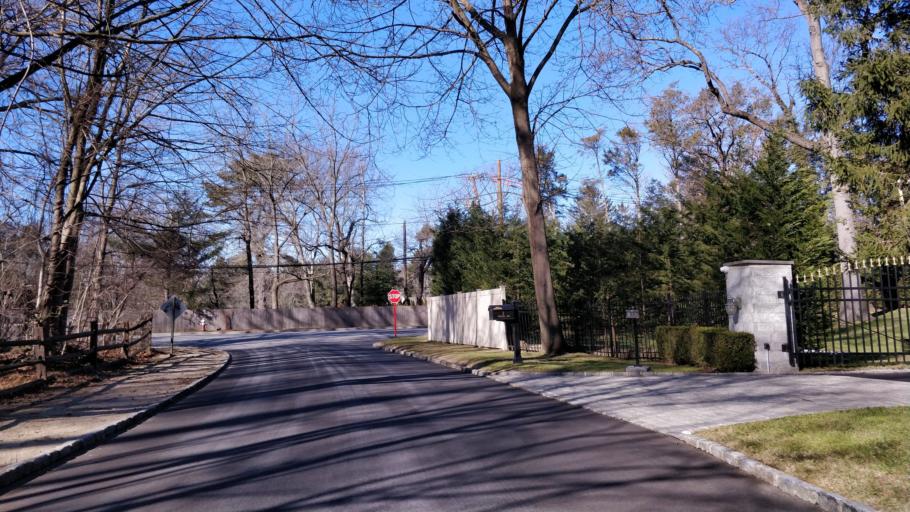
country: US
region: New York
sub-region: Nassau County
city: Brookville
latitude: 40.8156
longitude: -73.5738
